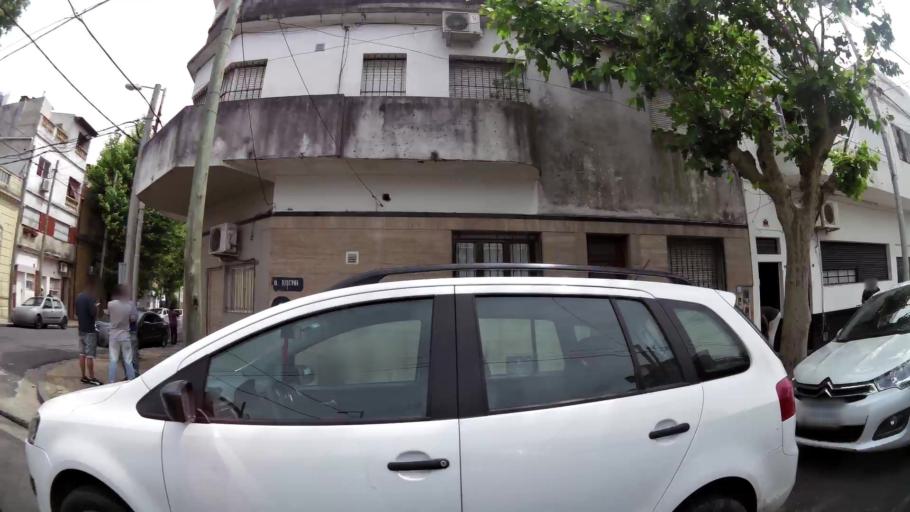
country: AR
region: Buenos Aires
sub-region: Partido de Avellaneda
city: Avellaneda
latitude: -34.6670
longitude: -58.3553
